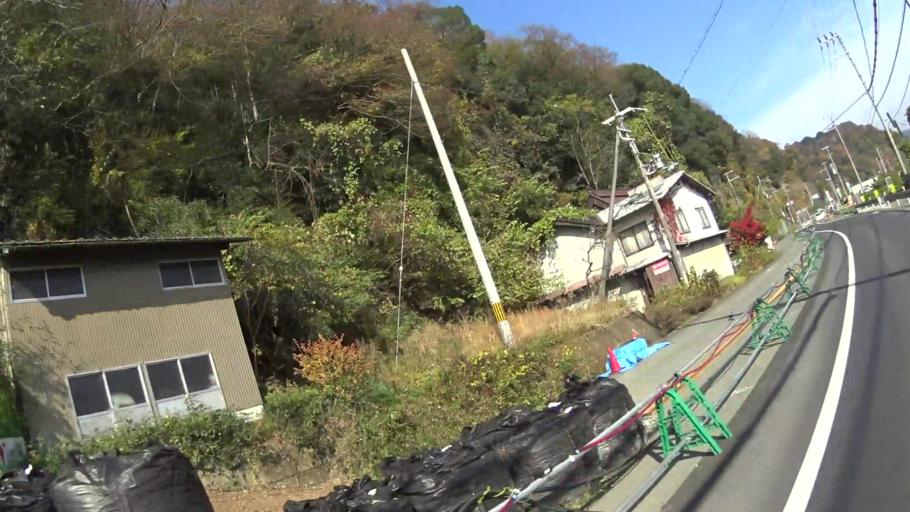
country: JP
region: Kyoto
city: Fukuchiyama
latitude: 35.3786
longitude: 135.1351
